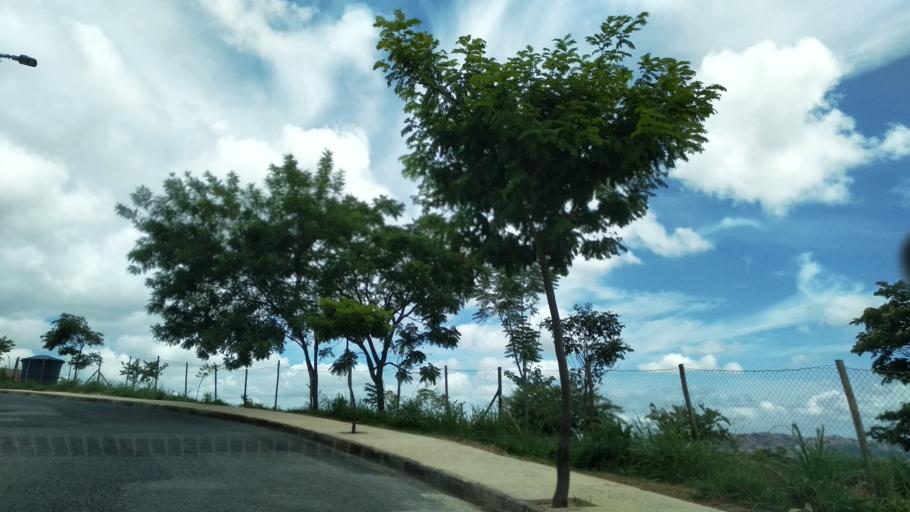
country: BR
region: Minas Gerais
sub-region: Belo Horizonte
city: Belo Horizonte
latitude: -19.8611
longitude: -43.8893
